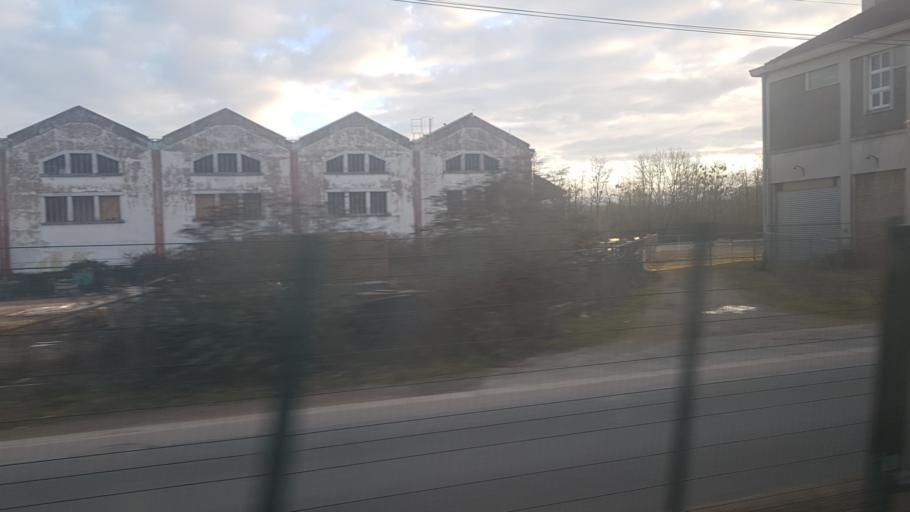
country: FR
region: Lorraine
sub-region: Departement des Vosges
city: Nomexy
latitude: 48.3055
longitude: 6.3893
